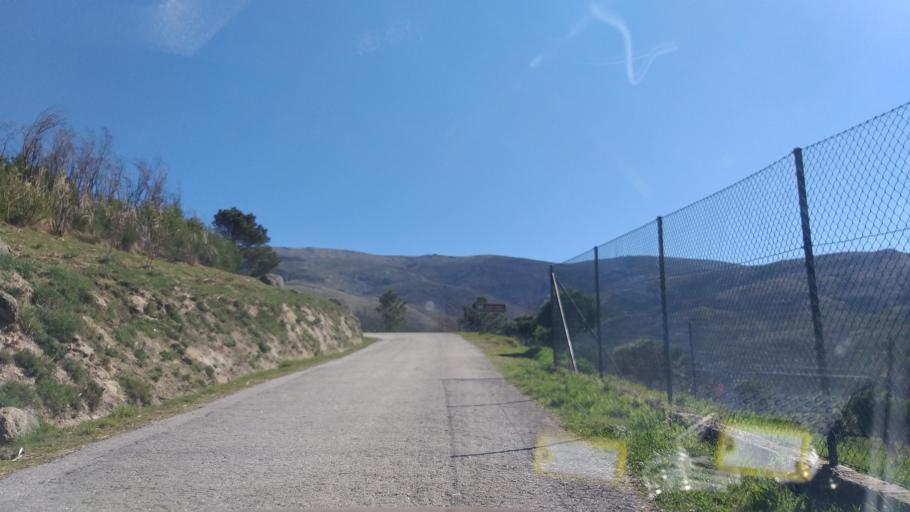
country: PT
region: Guarda
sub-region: Manteigas
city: Manteigas
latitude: 40.4913
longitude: -7.5816
